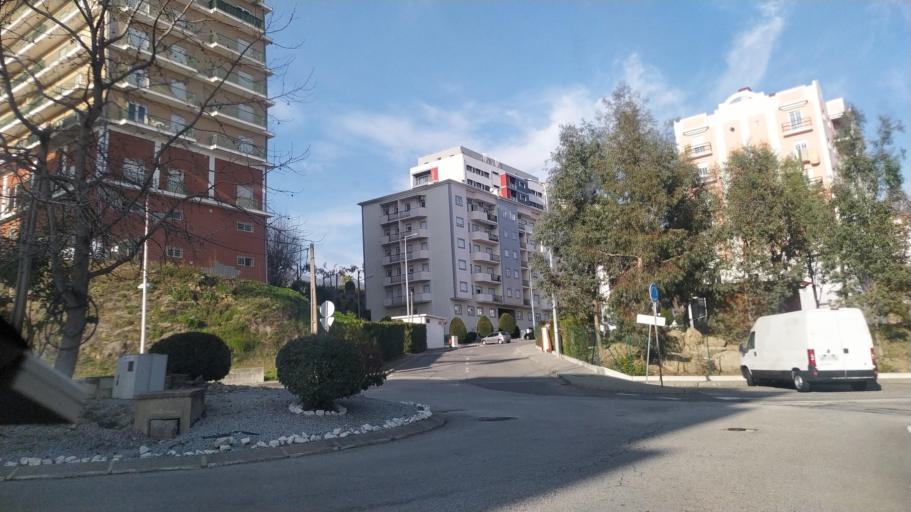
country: PT
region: Castelo Branco
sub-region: Covilha
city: Covilha
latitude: 40.2706
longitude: -7.5000
